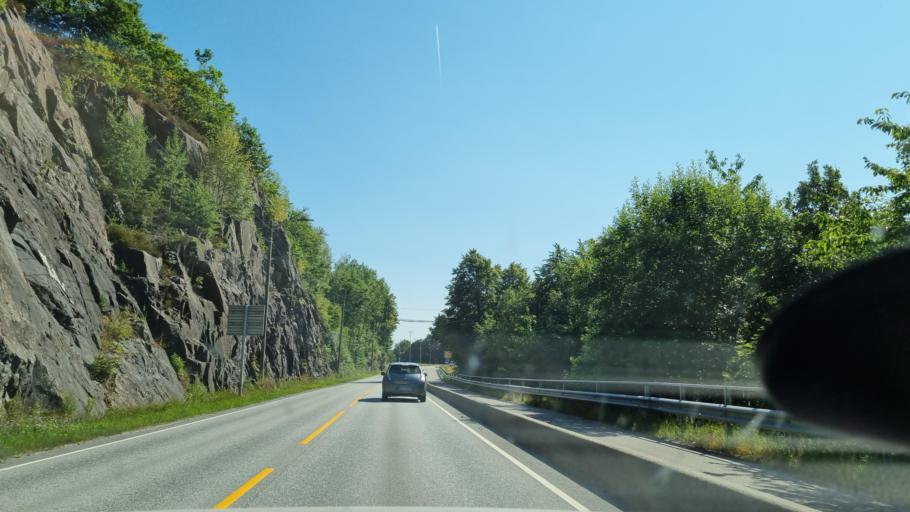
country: NO
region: Aust-Agder
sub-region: Arendal
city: Arendal
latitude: 58.4617
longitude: 8.8194
